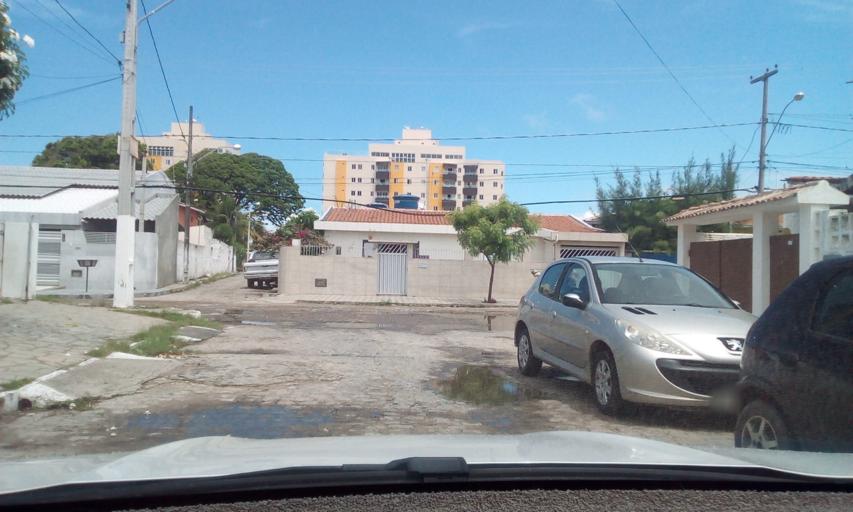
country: BR
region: Paraiba
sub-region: Cabedelo
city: Cabedelo
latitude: -6.9867
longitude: -34.8296
